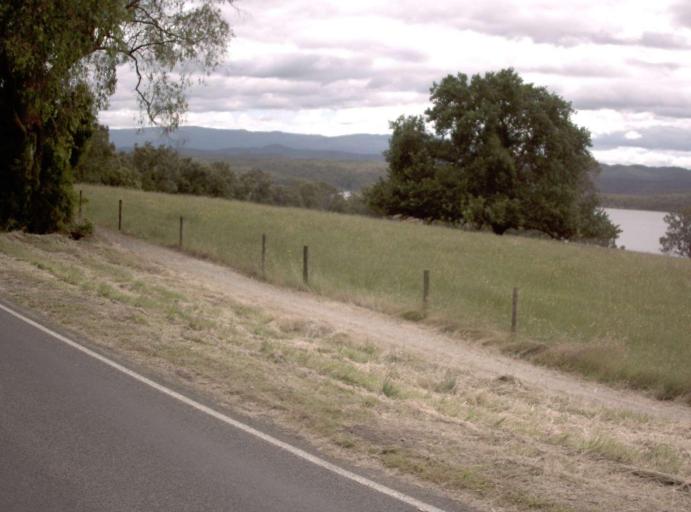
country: AU
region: Victoria
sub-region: Latrobe
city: Moe
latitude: -38.0649
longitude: 146.1740
